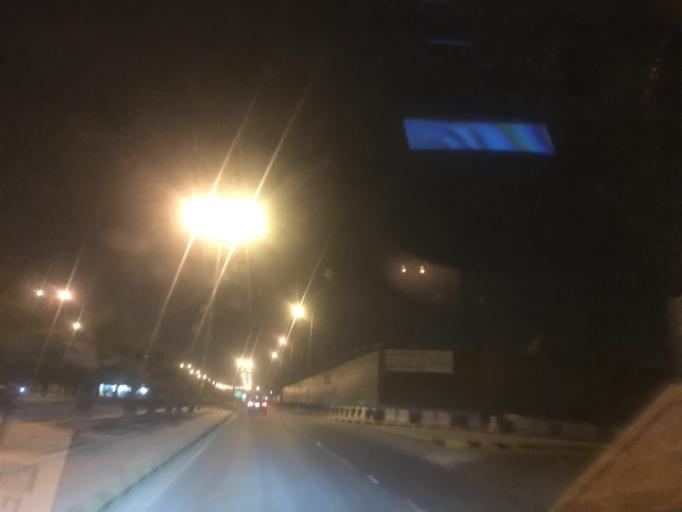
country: SA
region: Ar Riyad
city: Riyadh
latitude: 24.7912
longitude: 46.5882
